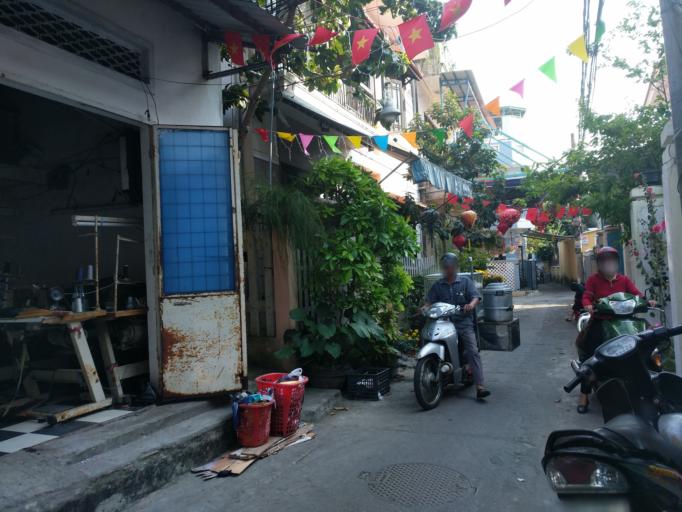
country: VN
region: Quang Nam
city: Hoi An
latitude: 15.8826
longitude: 108.3268
